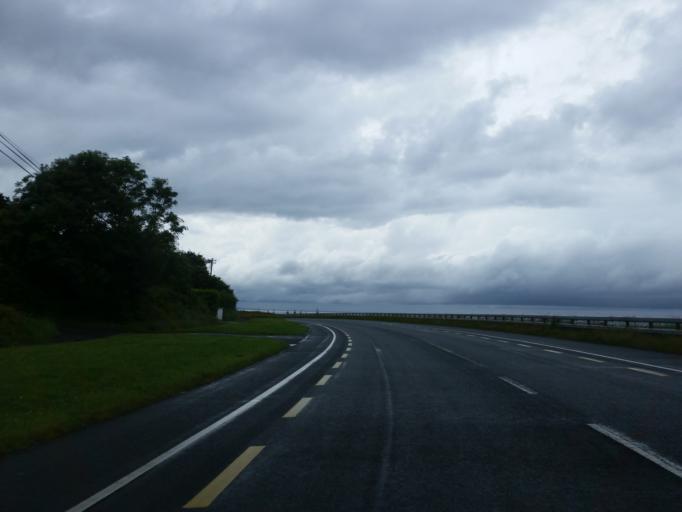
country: IE
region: Connaught
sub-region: Sligo
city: Strandhill
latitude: 54.2739
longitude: -8.5681
